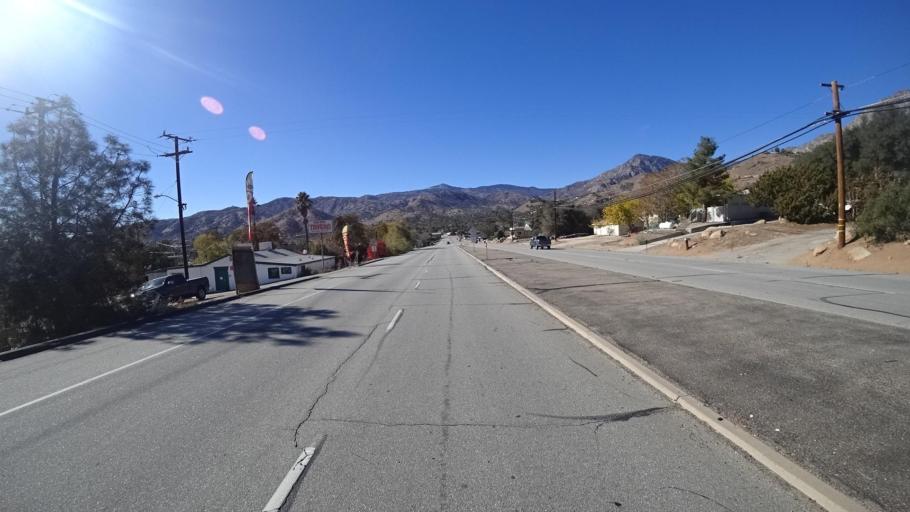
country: US
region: California
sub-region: Kern County
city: Wofford Heights
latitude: 35.7084
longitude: -118.4473
